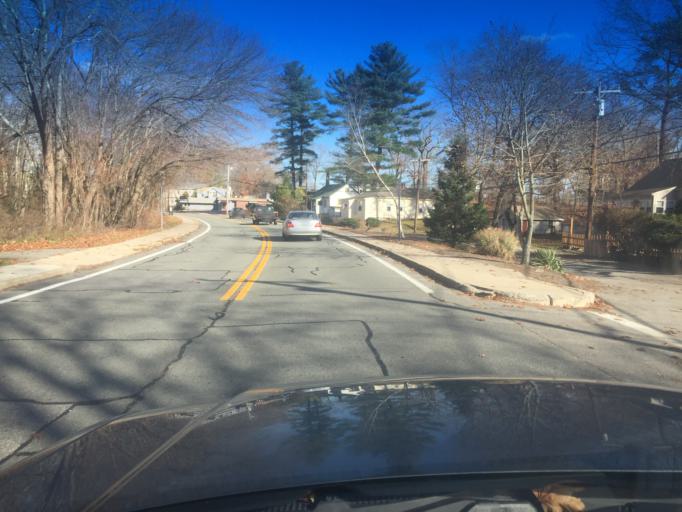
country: US
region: Rhode Island
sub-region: Providence County
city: Greenville
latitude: 41.8672
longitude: -71.5576
